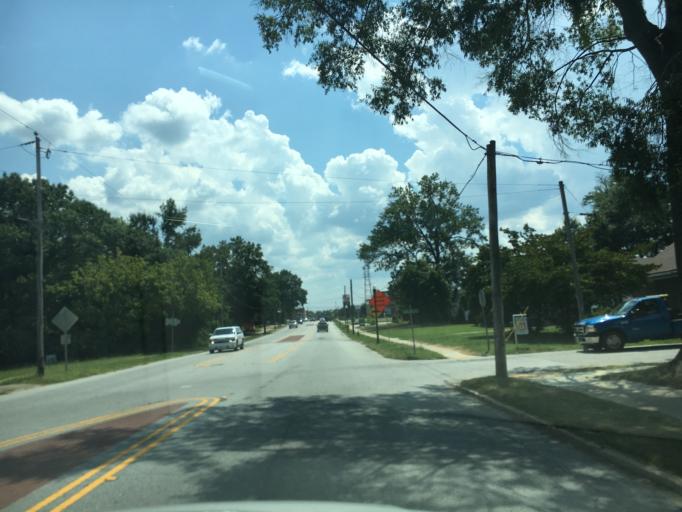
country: US
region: South Carolina
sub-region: Laurens County
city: Clinton
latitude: 34.4786
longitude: -81.8811
